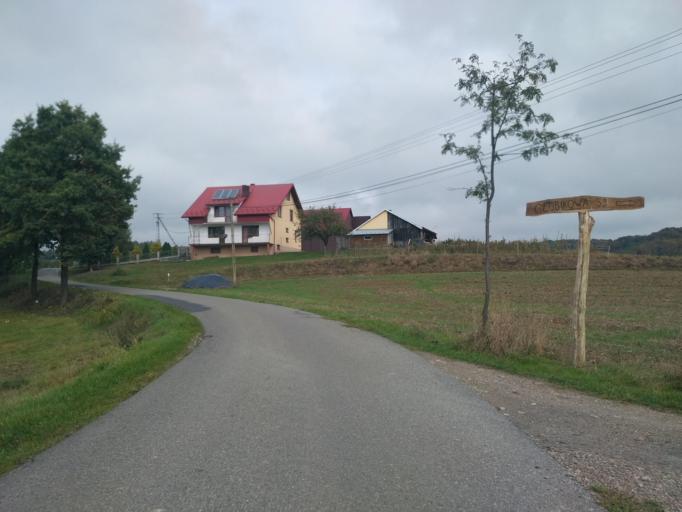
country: PL
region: Subcarpathian Voivodeship
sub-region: Powiat debicki
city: Brzostek
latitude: 49.9520
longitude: 21.4414
